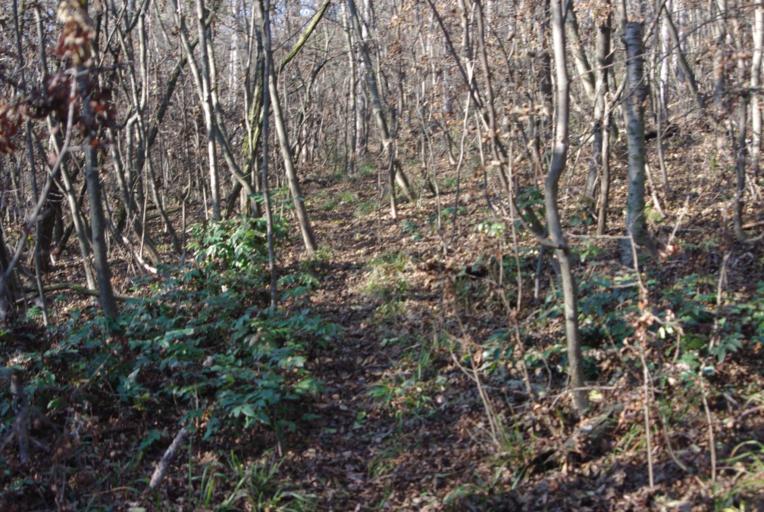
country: HU
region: Pest
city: Urom
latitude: 47.5844
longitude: 19.0328
